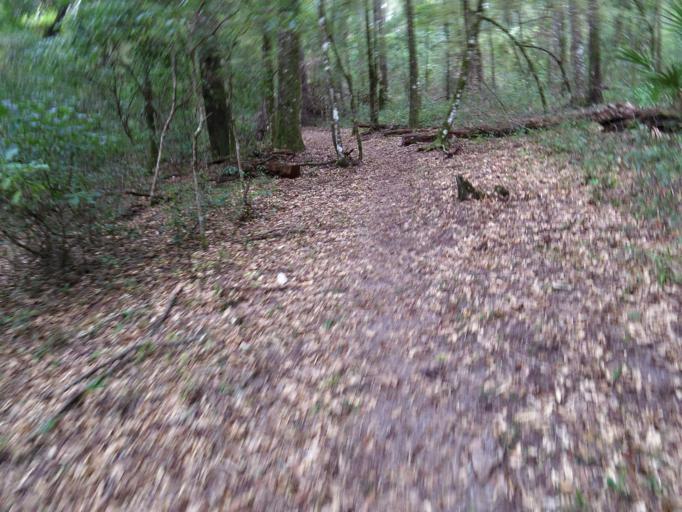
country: US
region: Florida
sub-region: Clay County
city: Middleburg
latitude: 30.1433
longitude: -81.9488
